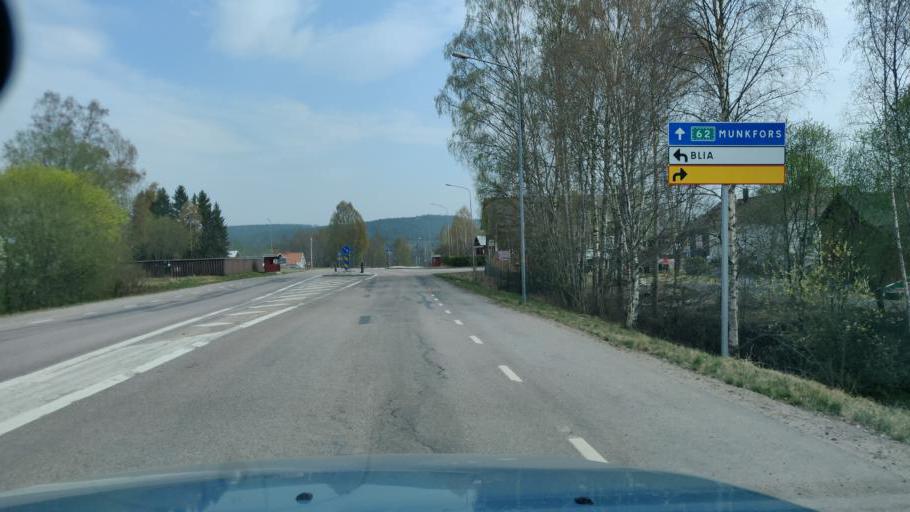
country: SE
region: Vaermland
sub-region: Munkfors Kommun
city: Munkfors
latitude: 59.8307
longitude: 13.5193
